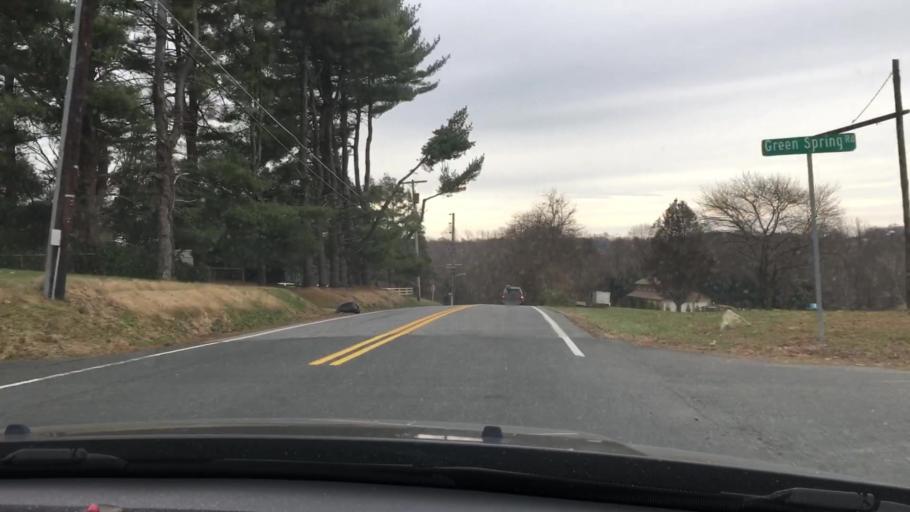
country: US
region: Maryland
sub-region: Harford County
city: Aberdeen
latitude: 39.5969
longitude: -76.1907
